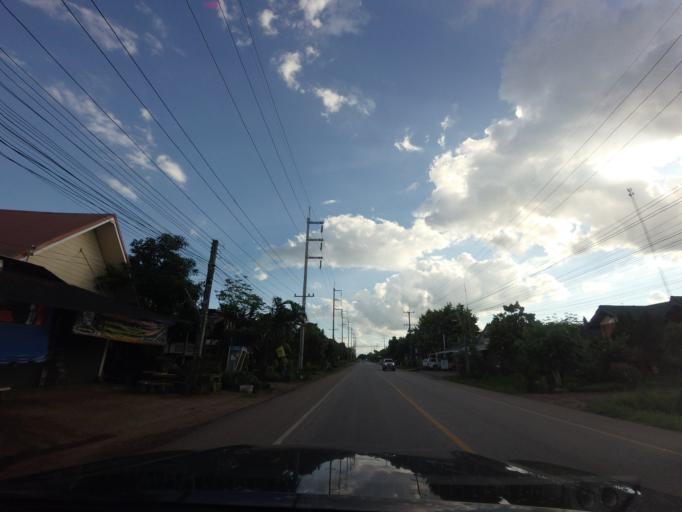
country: TH
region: Changwat Udon Thani
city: Thung Fon
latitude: 17.4565
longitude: 103.1876
